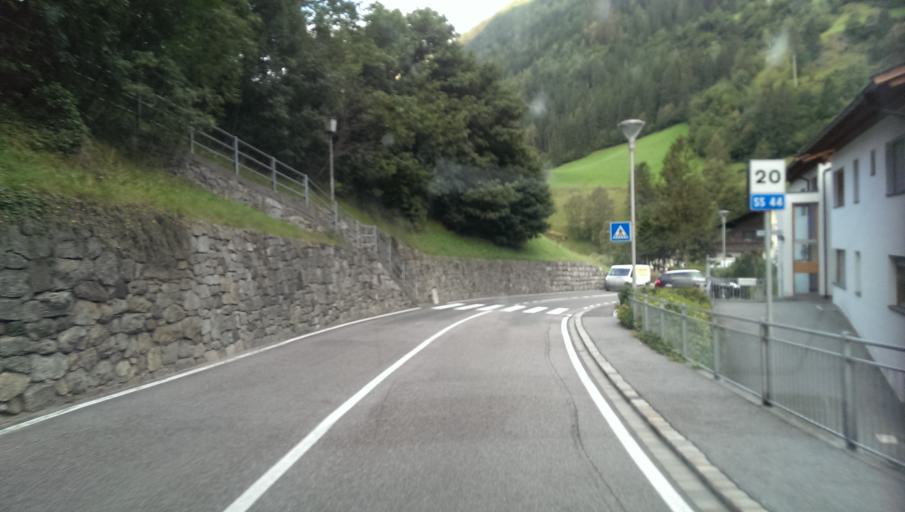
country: IT
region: Trentino-Alto Adige
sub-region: Bolzano
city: San Leonardo in Passiria
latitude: 46.8105
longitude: 11.2448
